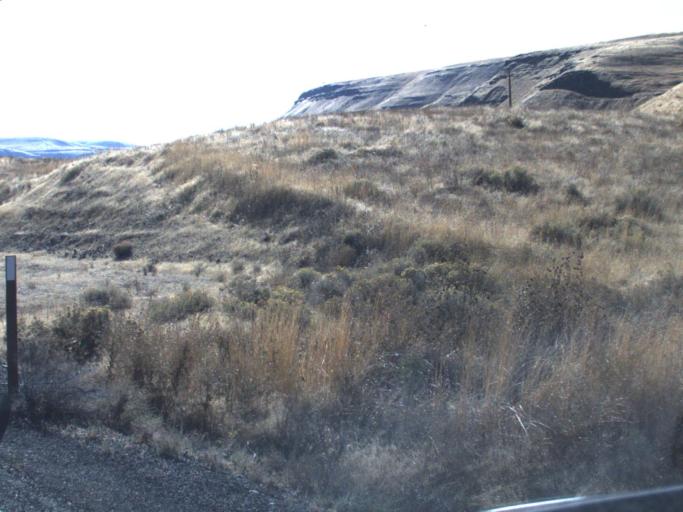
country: US
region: Washington
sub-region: Franklin County
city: Connell
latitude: 46.5722
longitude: -118.5348
